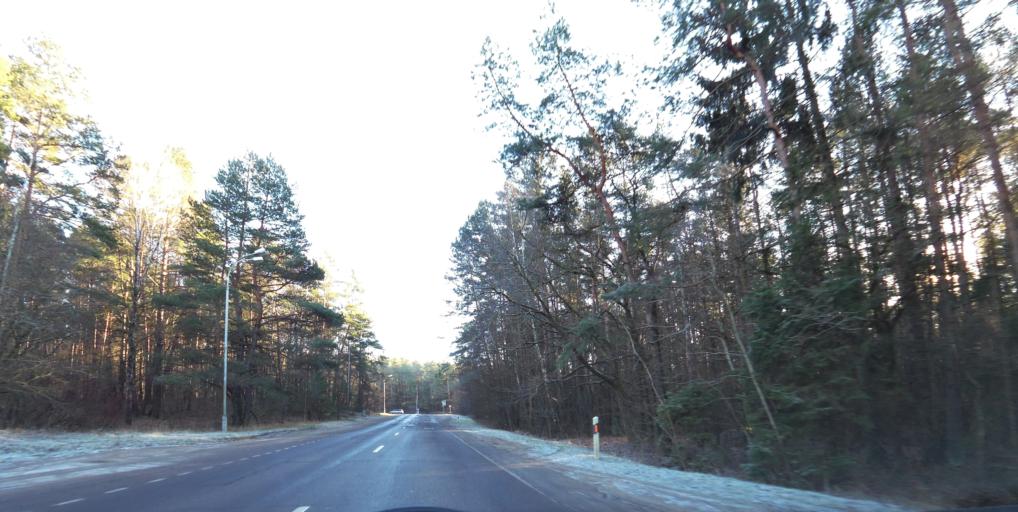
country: LT
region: Vilnius County
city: Lazdynai
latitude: 54.6406
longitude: 25.1770
